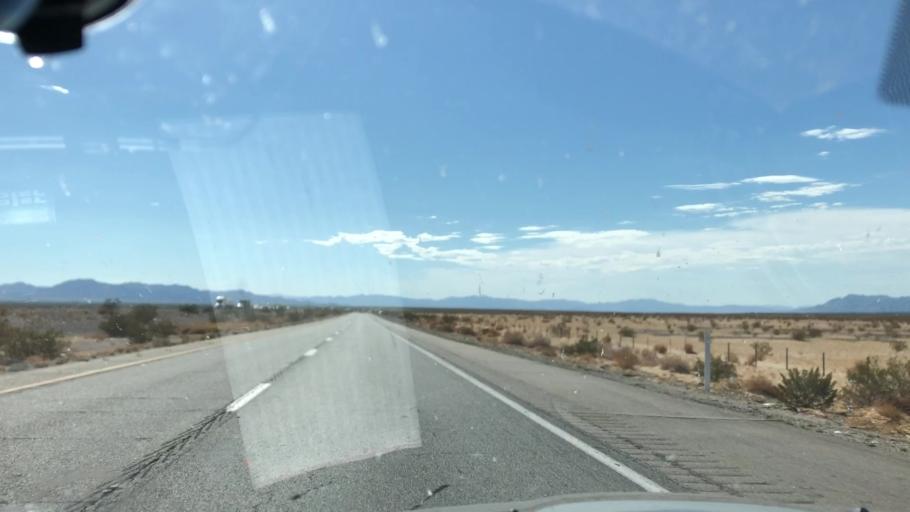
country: US
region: California
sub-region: Riverside County
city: Mesa Verde
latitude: 33.6369
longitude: -115.0846
